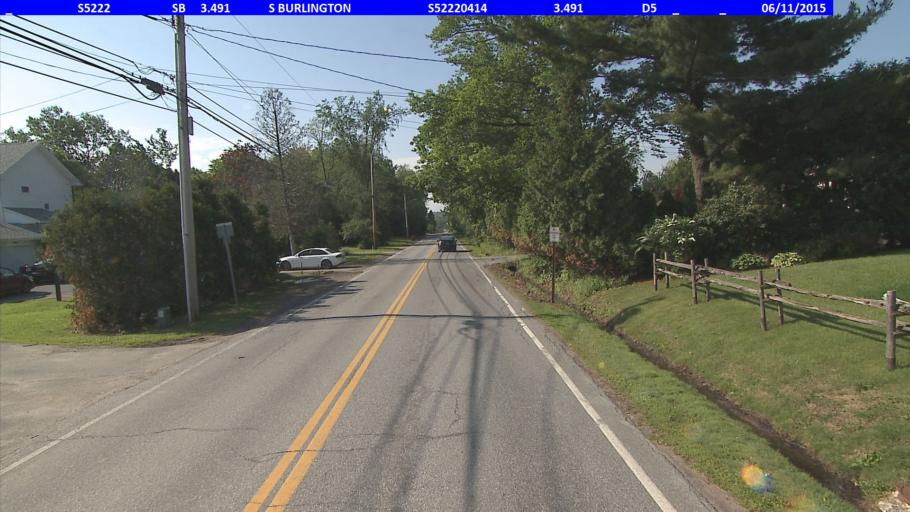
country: US
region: Vermont
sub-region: Chittenden County
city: South Burlington
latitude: 44.4666
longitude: -73.1915
